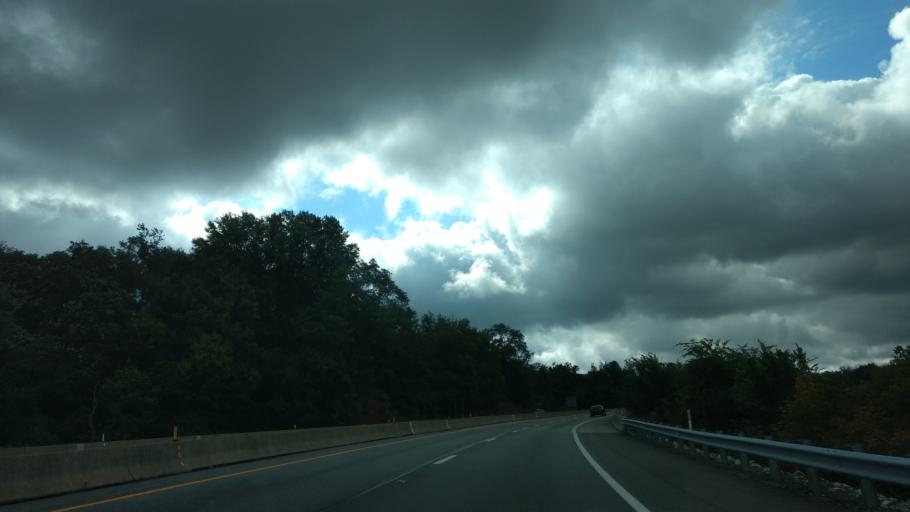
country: US
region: Pennsylvania
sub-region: Westmoreland County
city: Fellsburg
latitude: 40.1817
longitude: -79.8056
